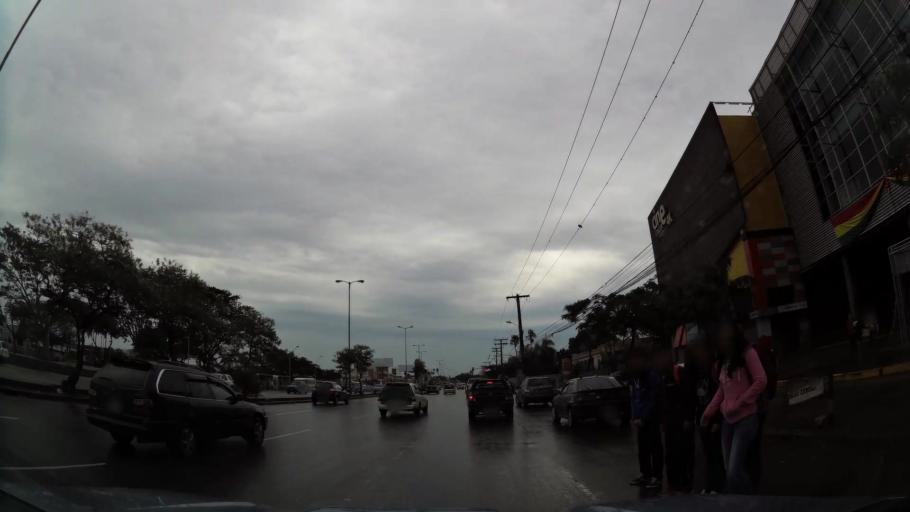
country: BO
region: Santa Cruz
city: Santa Cruz de la Sierra
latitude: -17.7989
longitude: -63.1789
